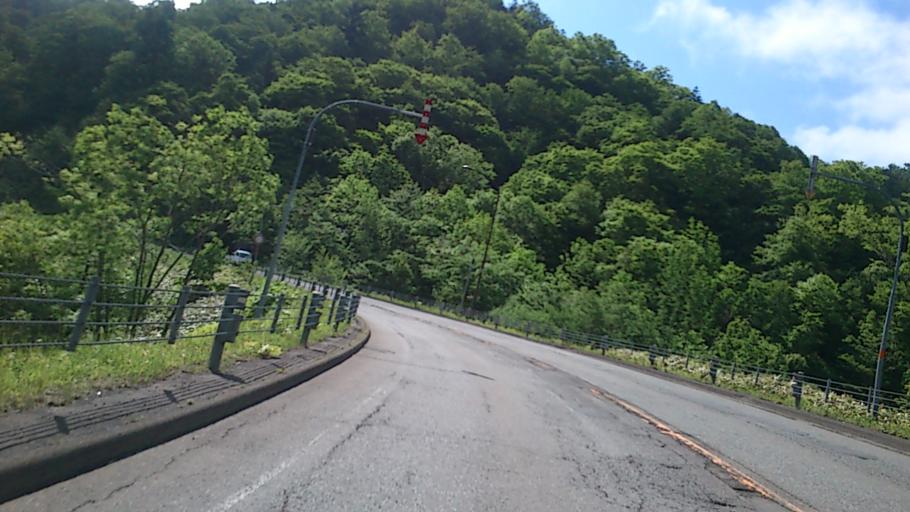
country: JP
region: Hokkaido
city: Shiraoi
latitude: 42.7164
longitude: 141.1984
